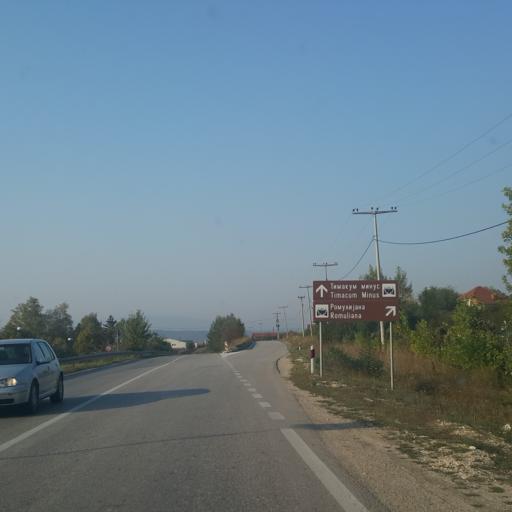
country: RS
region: Central Serbia
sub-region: Zajecarski Okrug
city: Zajecar
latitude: 43.9262
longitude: 22.2973
